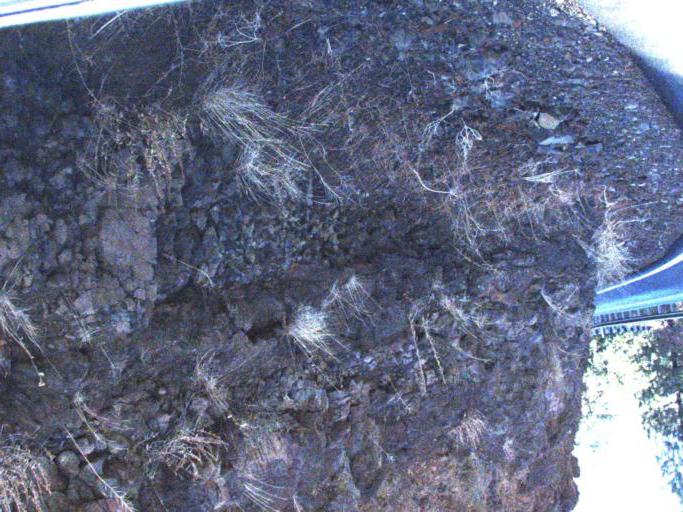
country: US
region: Washington
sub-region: Asotin County
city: Asotin
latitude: 46.0757
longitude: -117.2073
